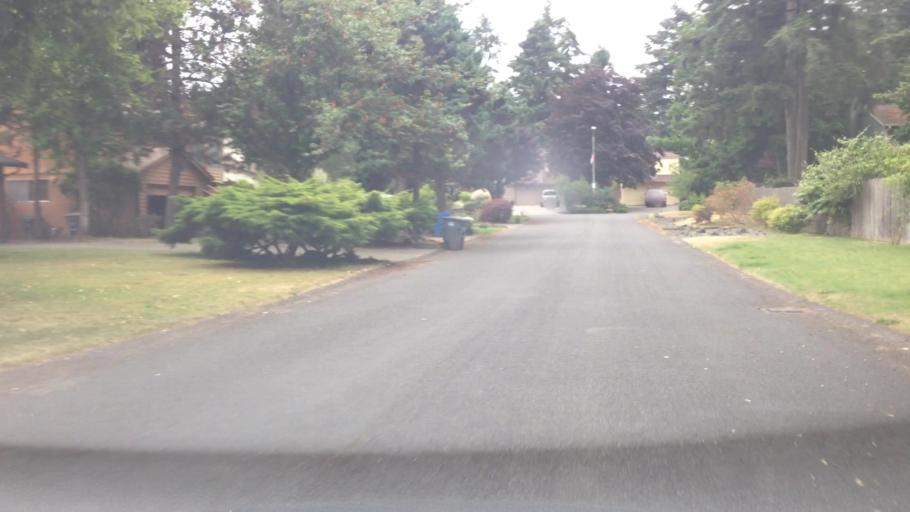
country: US
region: Washington
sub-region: Pierce County
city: South Hill
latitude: 47.1073
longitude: -122.2996
